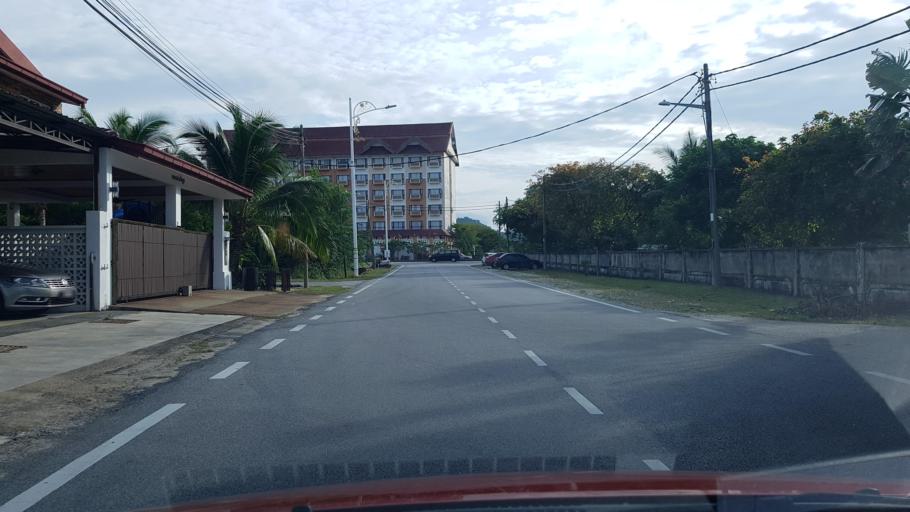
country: MY
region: Terengganu
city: Kuala Terengganu
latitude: 5.3164
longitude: 103.1554
